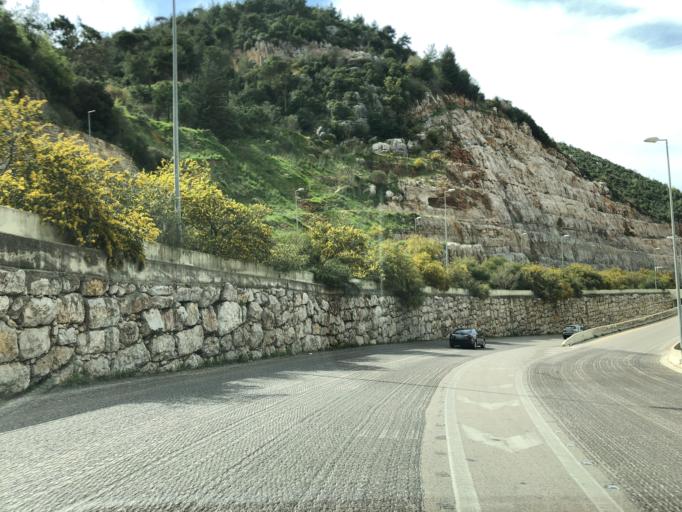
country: LB
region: Mont-Liban
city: Jdaidet el Matn
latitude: 33.8954
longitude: 35.6513
